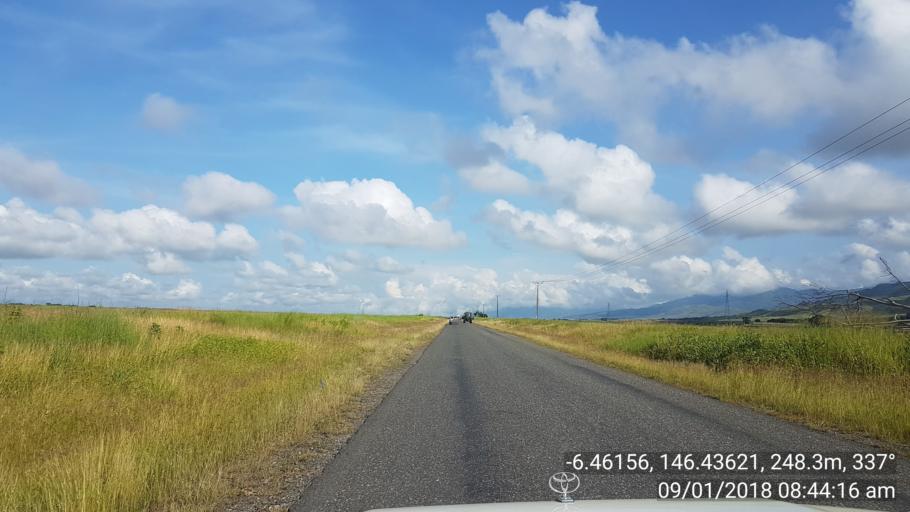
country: PG
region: Eastern Highlands
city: Kainantu
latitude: -6.4617
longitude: 146.4364
